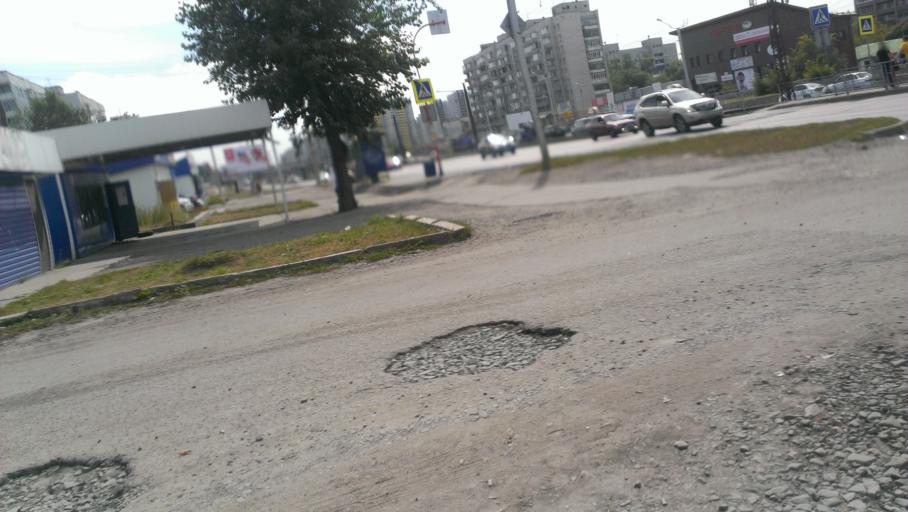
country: RU
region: Altai Krai
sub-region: Gorod Barnaulskiy
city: Barnaul
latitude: 53.3460
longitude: 83.6968
